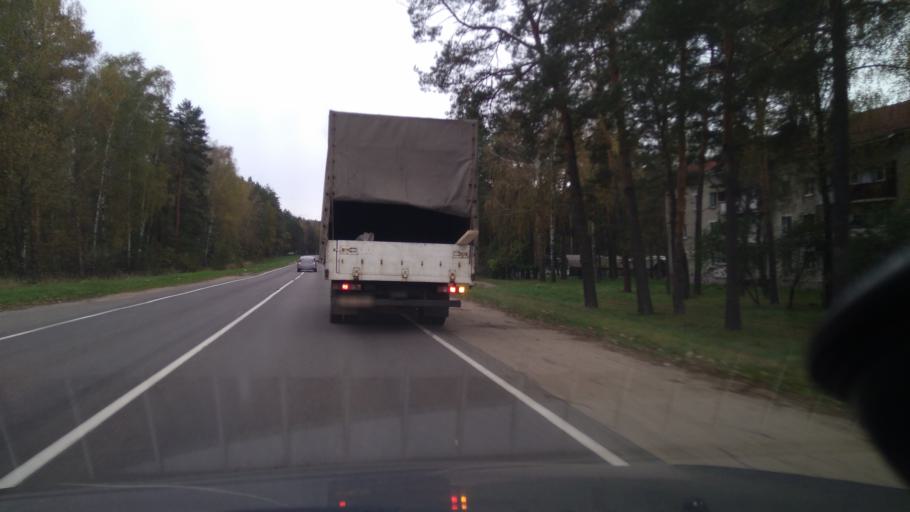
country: BY
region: Minsk
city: Svislach
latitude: 53.6435
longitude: 27.9123
